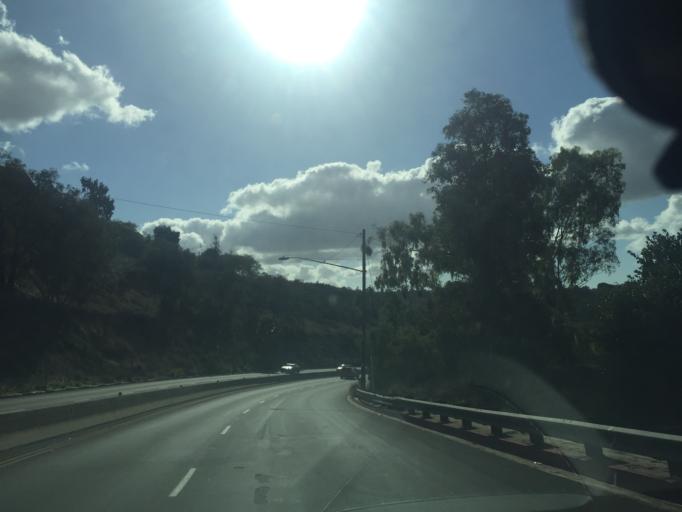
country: US
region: California
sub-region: San Diego County
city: La Mesa
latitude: 32.7878
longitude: -117.0846
